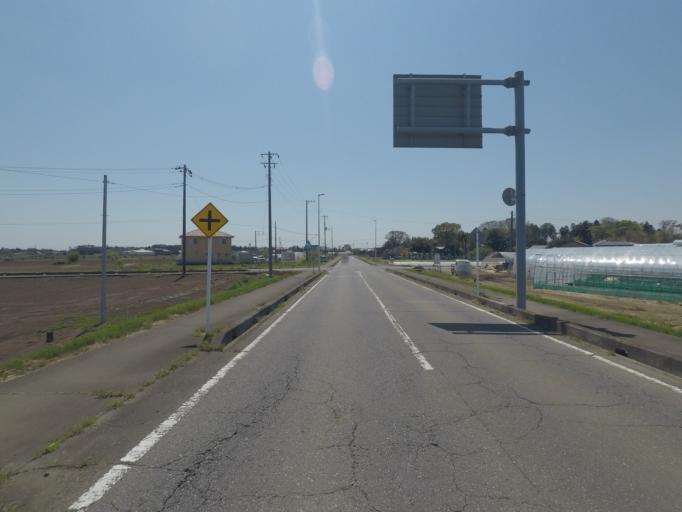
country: JP
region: Ibaraki
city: Ushiku
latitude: 35.9764
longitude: 140.0980
